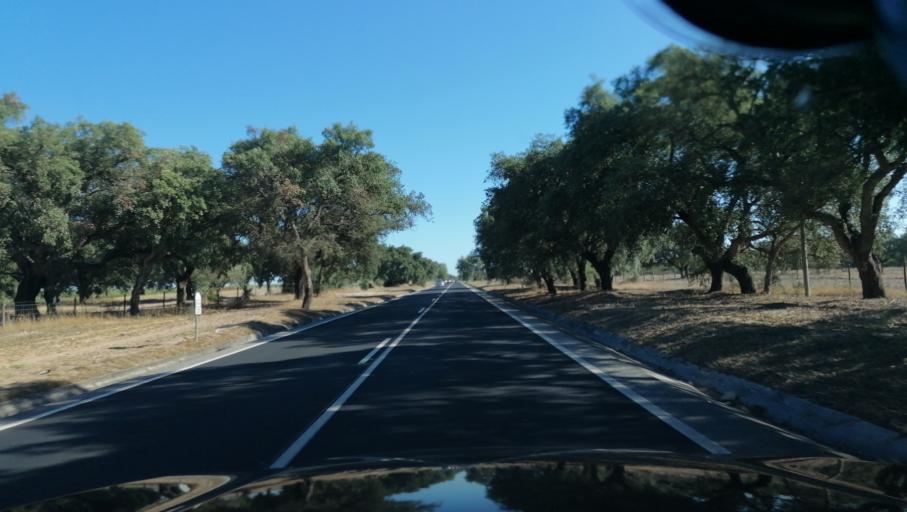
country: PT
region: Santarem
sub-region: Benavente
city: Poceirao
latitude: 38.8256
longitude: -8.8809
